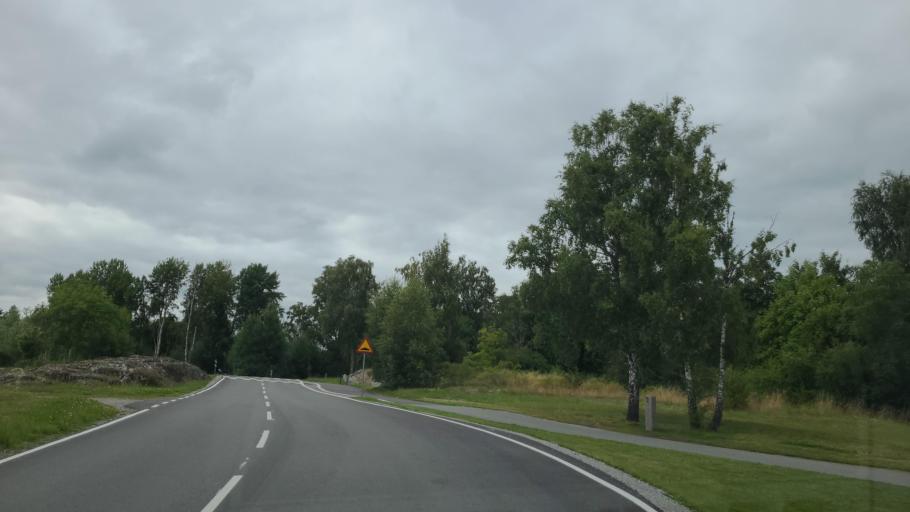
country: SE
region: Stockholm
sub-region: Upplands-Bro Kommun
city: Bro
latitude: 59.5010
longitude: 17.6263
